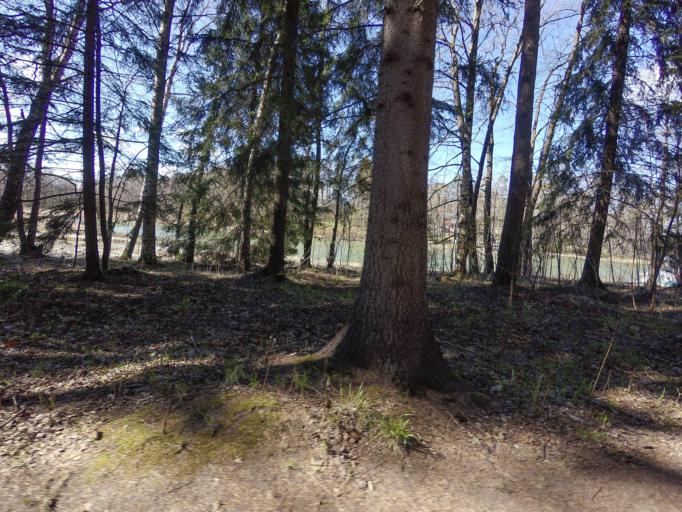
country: FI
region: Uusimaa
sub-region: Helsinki
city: Vantaa
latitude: 60.1723
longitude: 25.0630
